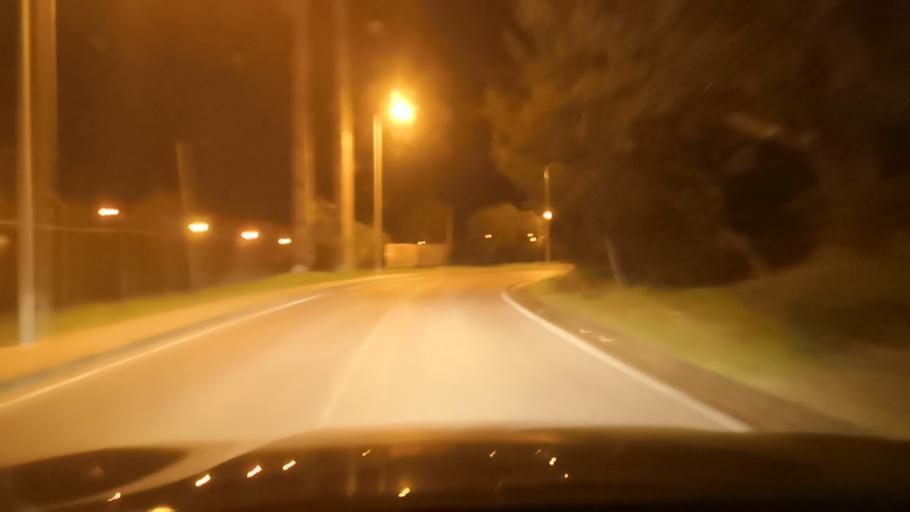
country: PT
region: Setubal
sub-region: Setubal
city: Setubal
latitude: 38.5487
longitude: -8.8794
